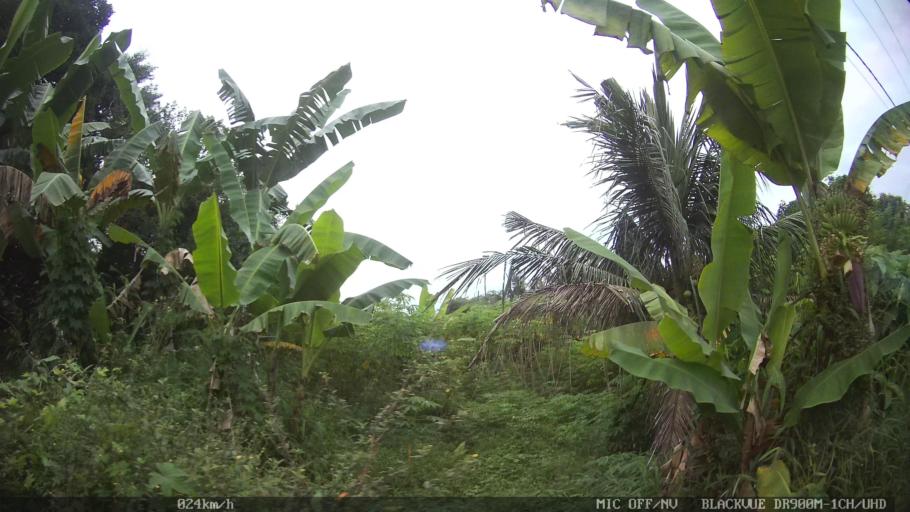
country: ID
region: North Sumatra
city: Sunggal
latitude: 3.6617
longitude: 98.5896
